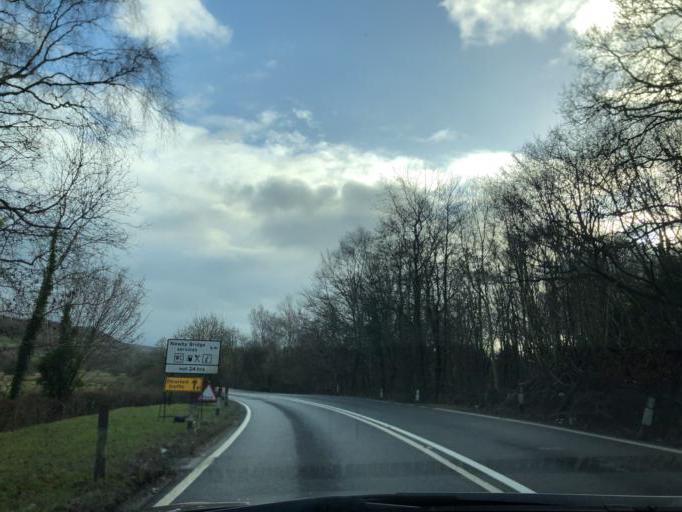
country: GB
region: England
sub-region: Cumbria
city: Grange-over-Sands
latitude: 54.2652
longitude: -2.9655
